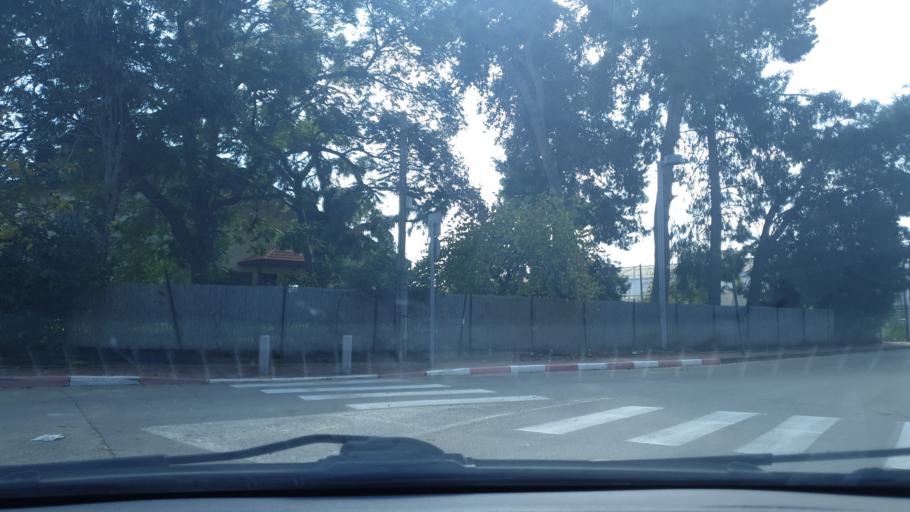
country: IL
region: Central District
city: Bet Dagan
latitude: 32.0076
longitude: 34.8199
